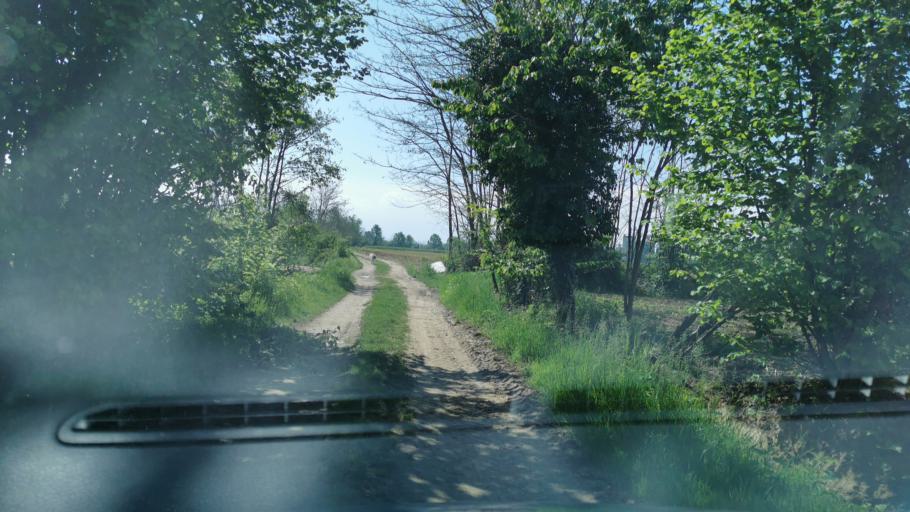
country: IT
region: Piedmont
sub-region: Provincia di Torino
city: Feletto
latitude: 45.2865
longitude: 7.7204
